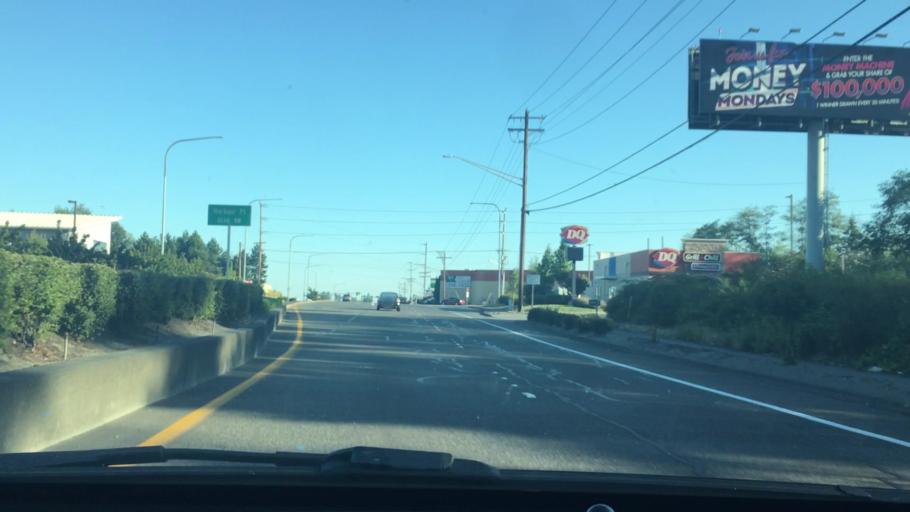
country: US
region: Washington
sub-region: Snohomish County
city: Martha Lake
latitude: 47.8872
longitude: -122.2831
